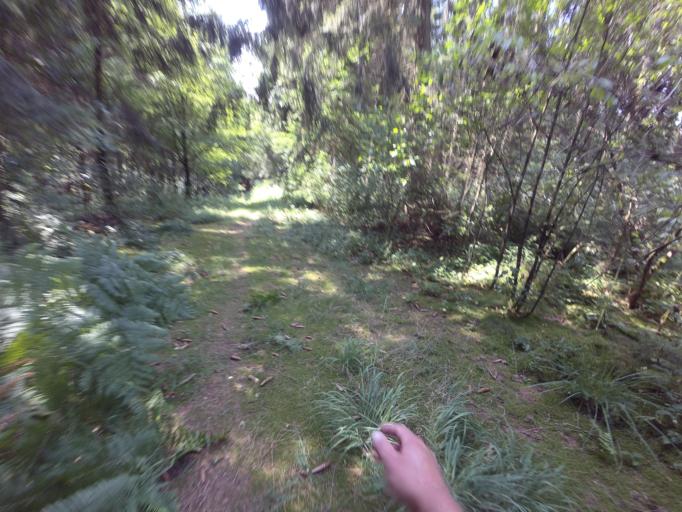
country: BE
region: Wallonia
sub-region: Province de Liege
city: Lontzen
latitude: 50.6956
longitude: 6.0067
